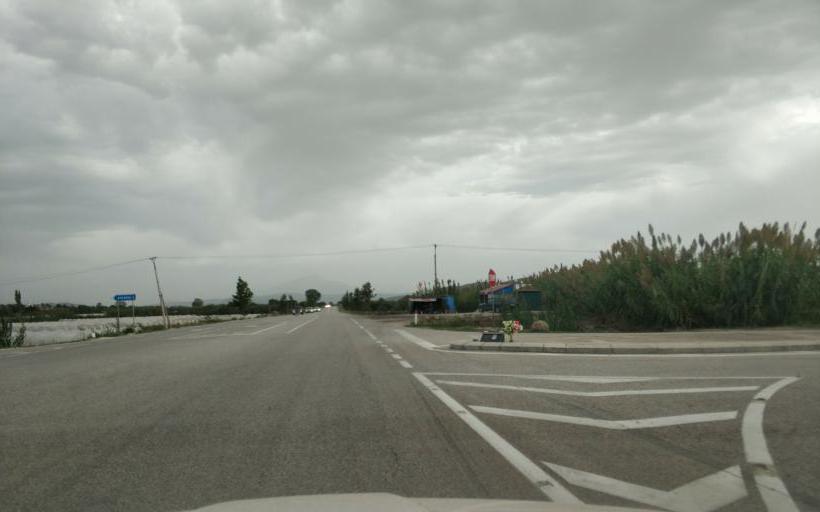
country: AL
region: Fier
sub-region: Rrethi i Fierit
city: Frakulla e Madhe
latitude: 40.6309
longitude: 19.5086
